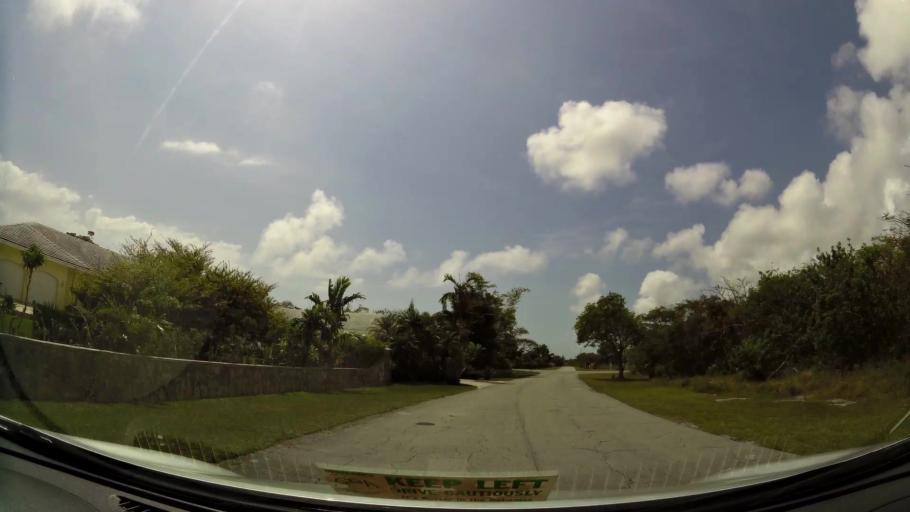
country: BS
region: Freeport
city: Freeport
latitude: 26.5091
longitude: -78.7082
